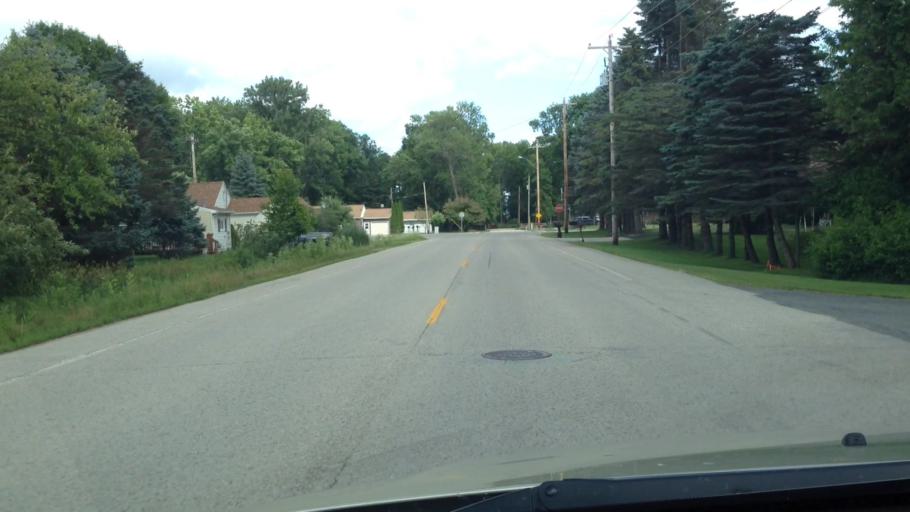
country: US
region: Michigan
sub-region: Menominee County
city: Menominee
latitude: 45.1439
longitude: -87.6048
